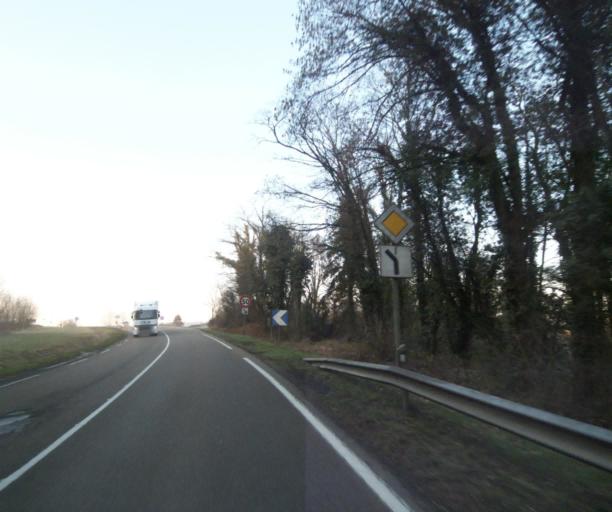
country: FR
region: Champagne-Ardenne
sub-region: Departement de la Haute-Marne
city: Bienville
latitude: 48.6012
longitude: 5.0334
